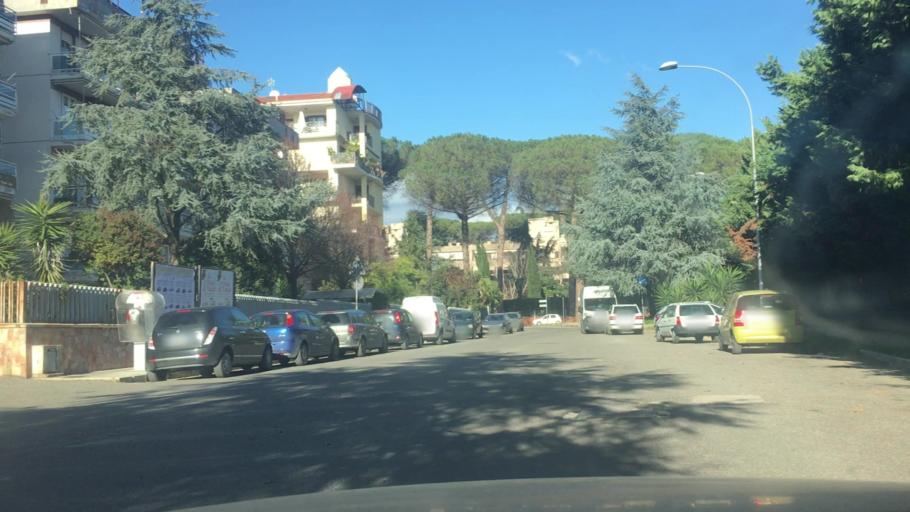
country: IT
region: Campania
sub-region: Provincia di Caserta
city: Caserta
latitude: 41.0724
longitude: 14.3542
